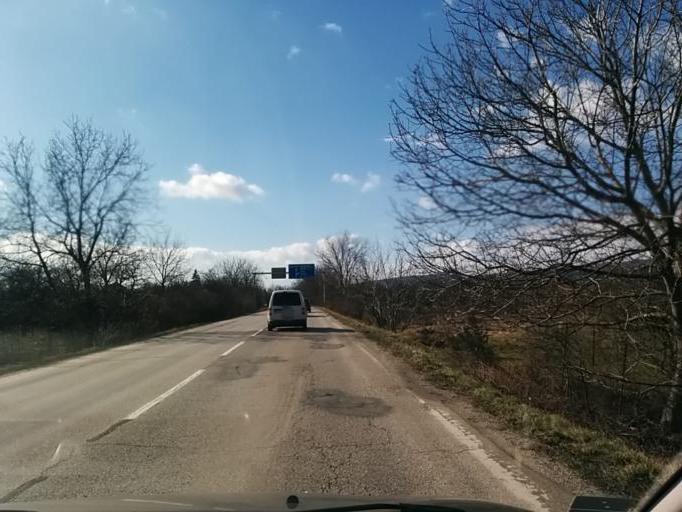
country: SK
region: Trenciansky
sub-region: Okres Nove Mesto nad Vahom
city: Nove Mesto nad Vahom
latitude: 48.7693
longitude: 17.8471
